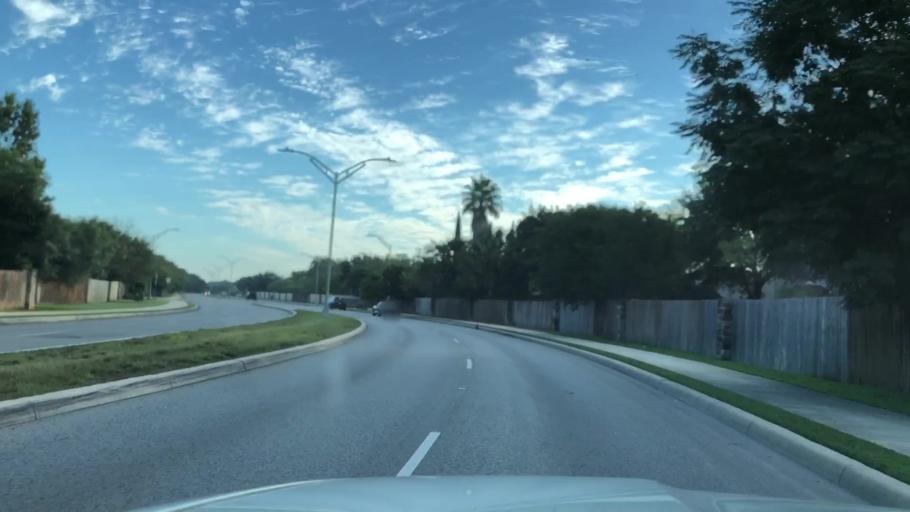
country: US
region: Texas
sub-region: Bexar County
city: Leon Valley
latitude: 29.5417
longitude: -98.6295
